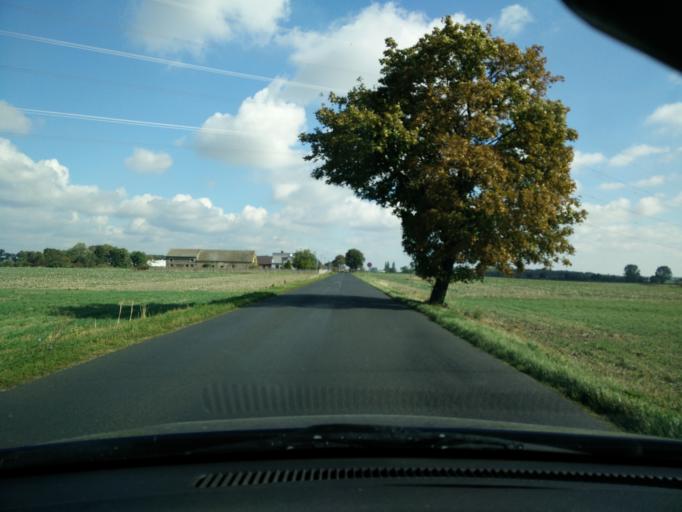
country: PL
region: Greater Poland Voivodeship
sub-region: Powiat sredzki
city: Dominowo
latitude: 52.2978
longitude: 17.3416
